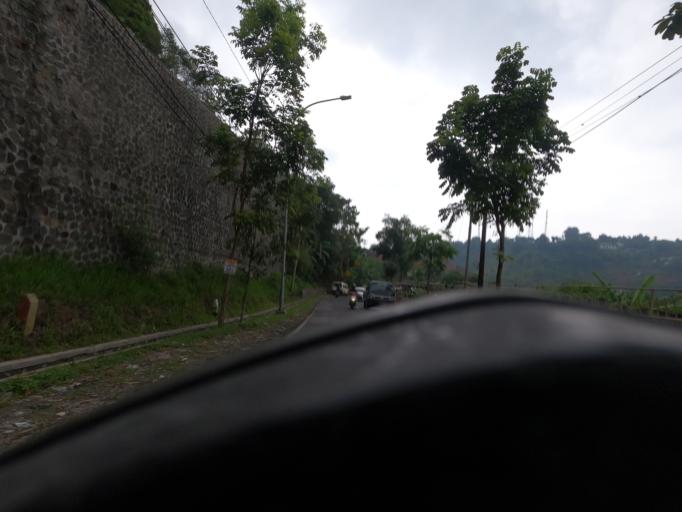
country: ID
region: West Java
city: Lembang
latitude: -6.8201
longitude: 107.6087
